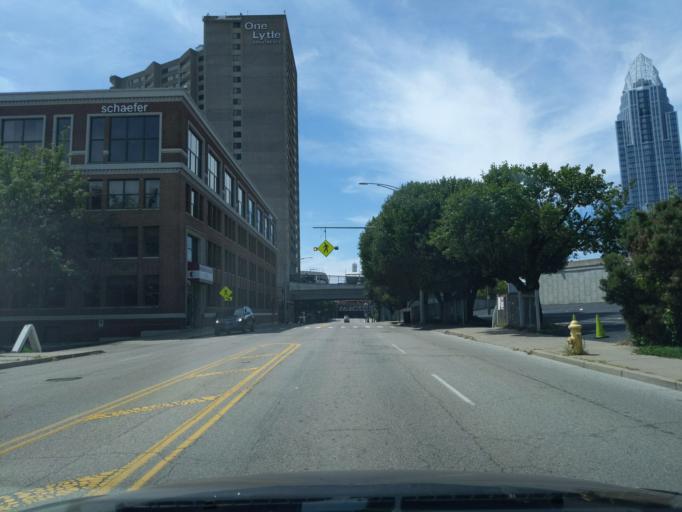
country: US
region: Kentucky
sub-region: Campbell County
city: Newport
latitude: 39.1006
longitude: -84.5015
